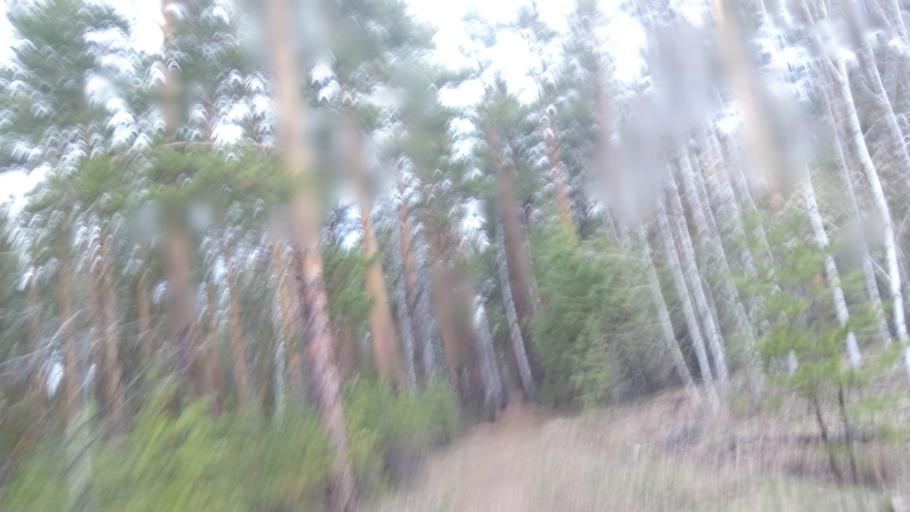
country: RU
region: Chelyabinsk
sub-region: Gorod Chelyabinsk
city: Chelyabinsk
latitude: 55.1349
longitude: 61.3375
